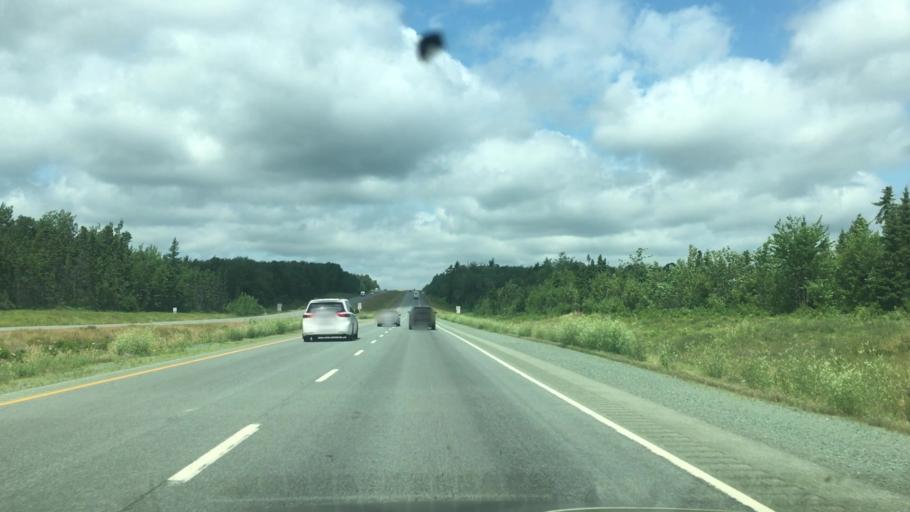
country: CA
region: Nova Scotia
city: Springhill
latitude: 45.6985
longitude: -64.0228
